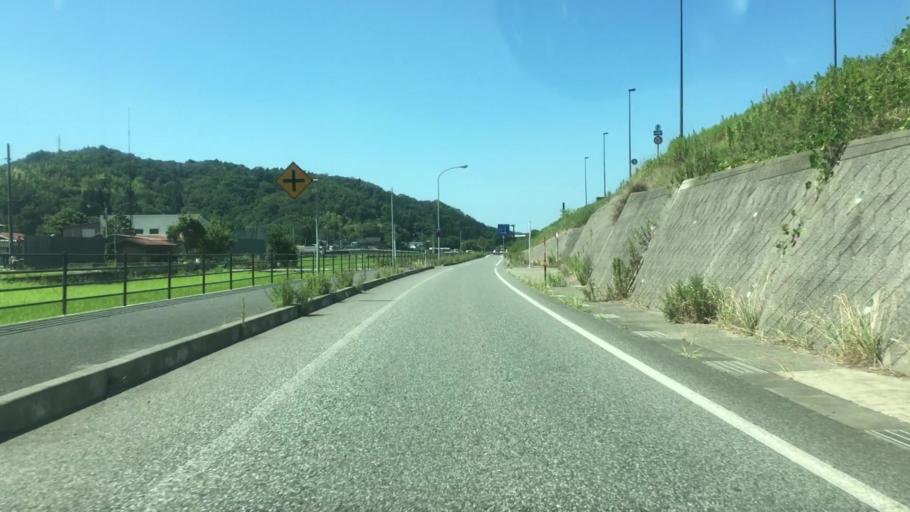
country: JP
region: Tottori
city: Tottori
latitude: 35.4316
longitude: 134.2053
